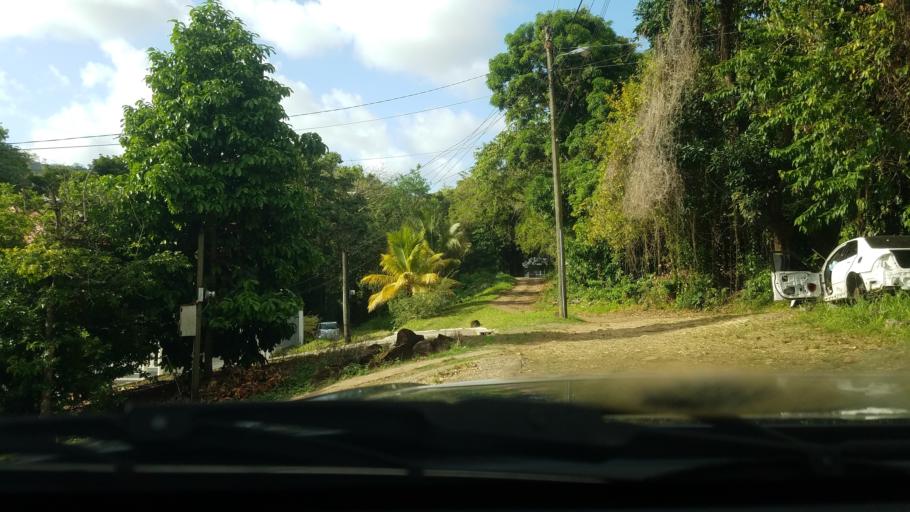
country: LC
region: Castries Quarter
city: Bisee
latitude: 14.0363
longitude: -60.9536
